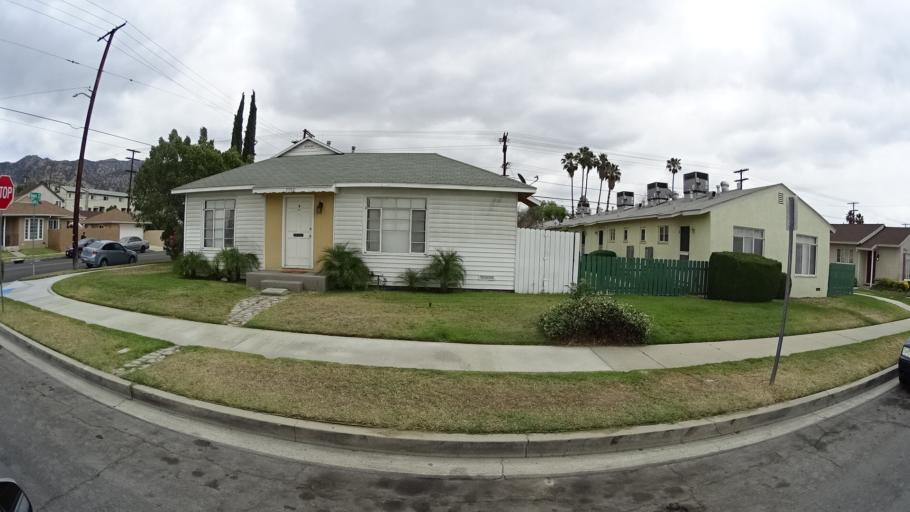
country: US
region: California
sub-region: Los Angeles County
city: Burbank
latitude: 34.2026
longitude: -118.3368
